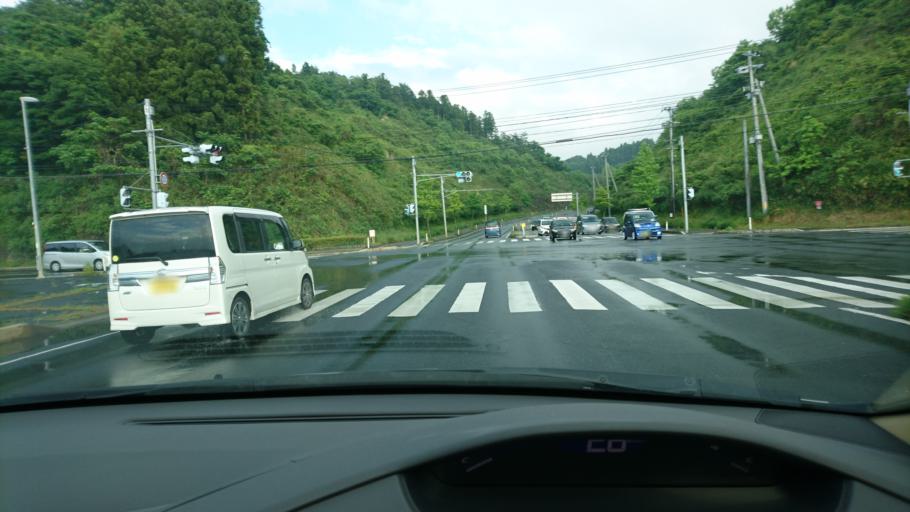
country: JP
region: Iwate
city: Ichinoseki
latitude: 38.9341
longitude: 141.1641
